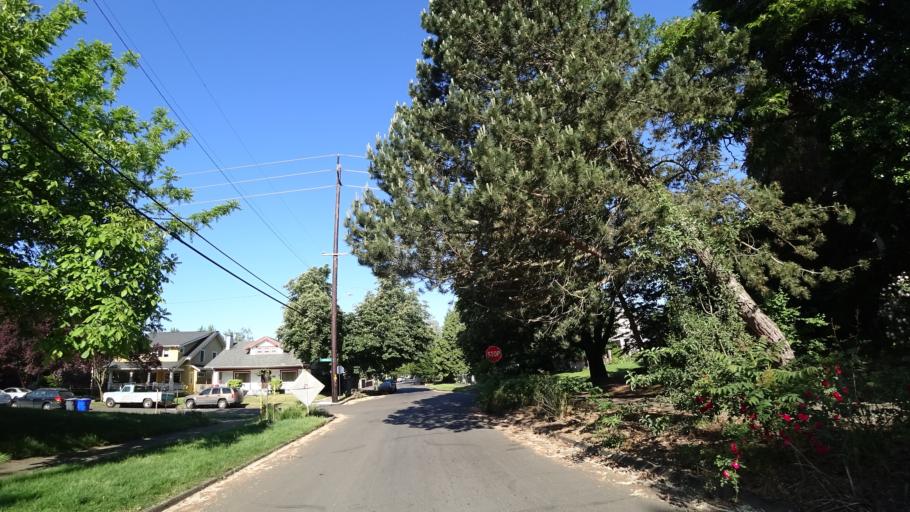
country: US
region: Oregon
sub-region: Multnomah County
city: Portland
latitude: 45.5652
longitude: -122.6666
